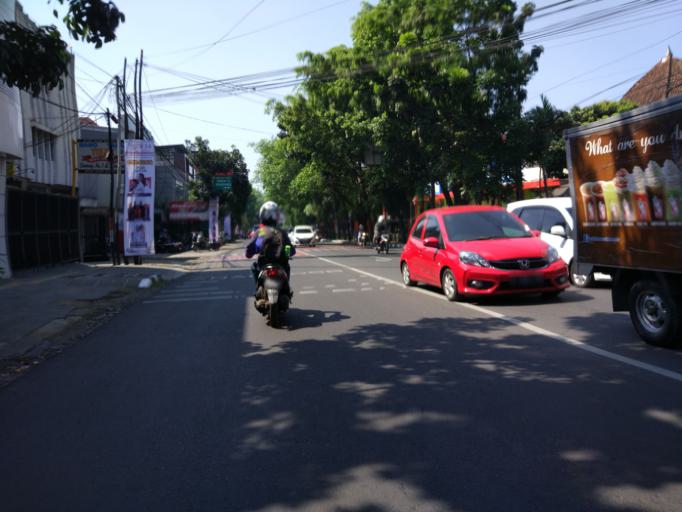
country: ID
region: West Java
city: Bandung
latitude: -6.9224
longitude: 107.6182
